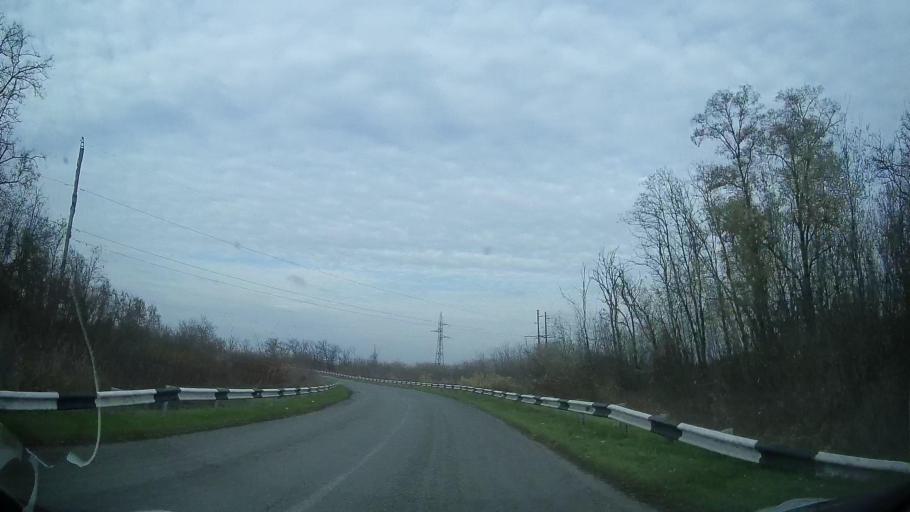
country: RU
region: Rostov
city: Zernograd
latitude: 46.8837
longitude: 40.3414
